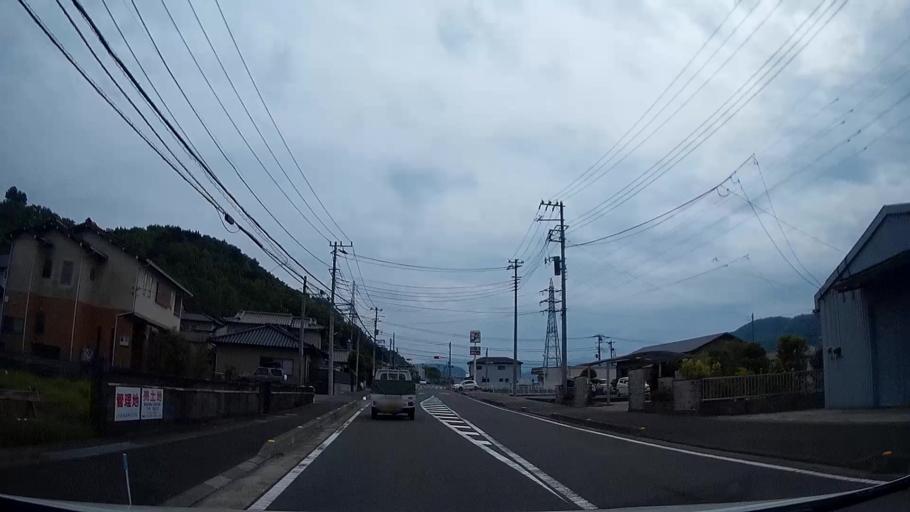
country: JP
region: Shizuoka
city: Ito
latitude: 34.9720
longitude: 138.9499
